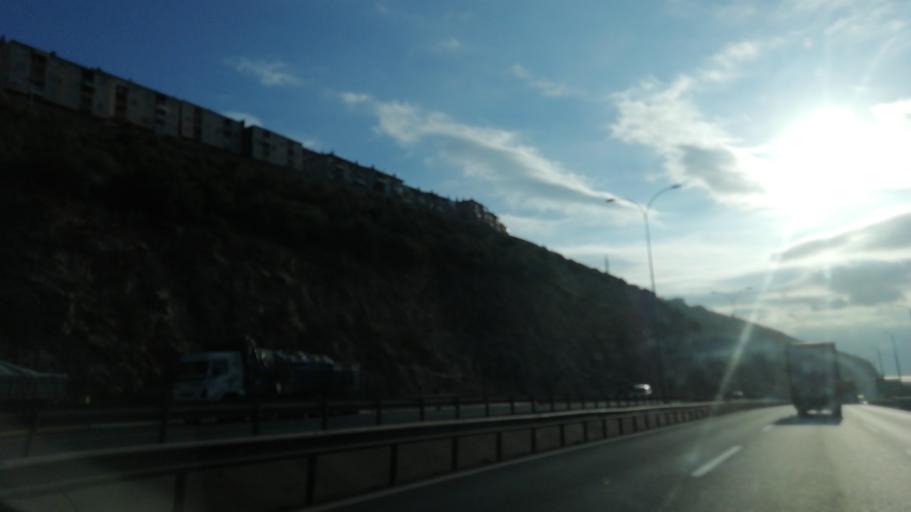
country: TR
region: Kocaeli
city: Hereke
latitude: 40.7852
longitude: 29.6238
